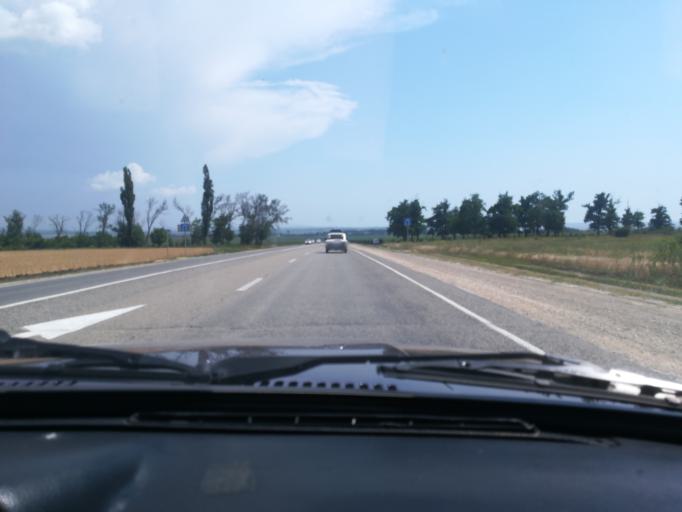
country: RU
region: Krasnodarskiy
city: Vinogradnyy
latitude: 45.0838
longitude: 37.3178
